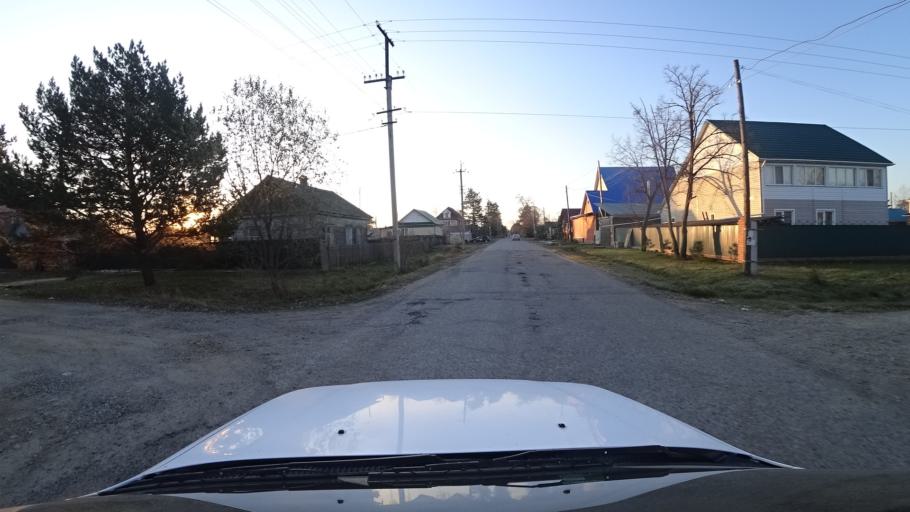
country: RU
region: Primorskiy
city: Dal'nerechensk
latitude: 45.9264
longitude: 133.7323
